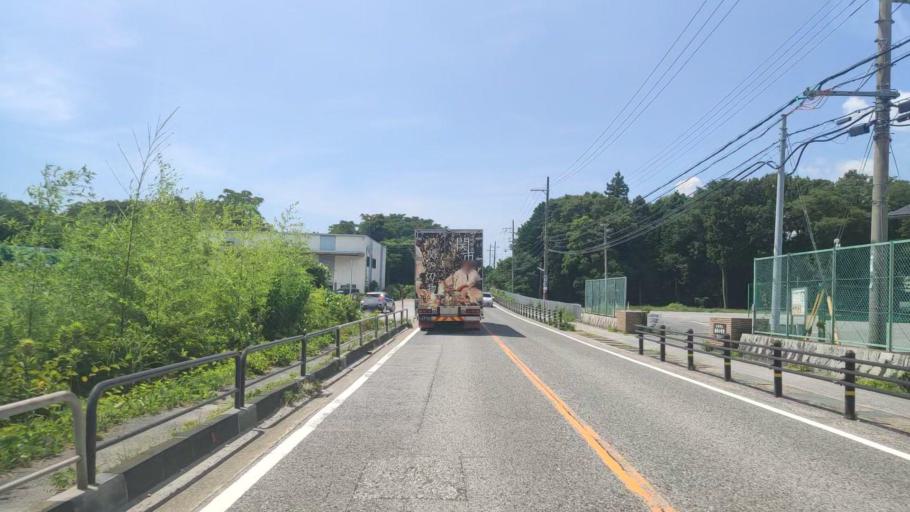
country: JP
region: Shiga Prefecture
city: Nagahama
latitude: 35.3742
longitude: 136.3855
